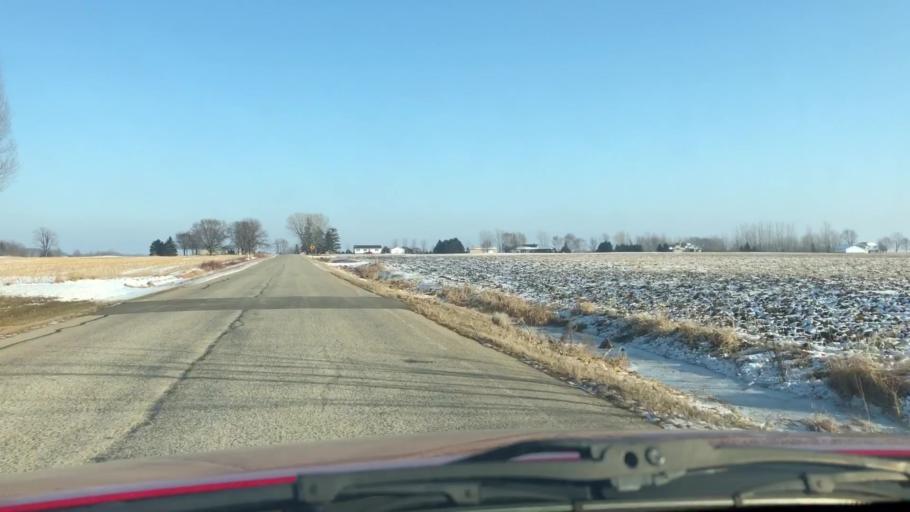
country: US
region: Wisconsin
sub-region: Outagamie County
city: Seymour
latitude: 44.4869
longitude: -88.3146
